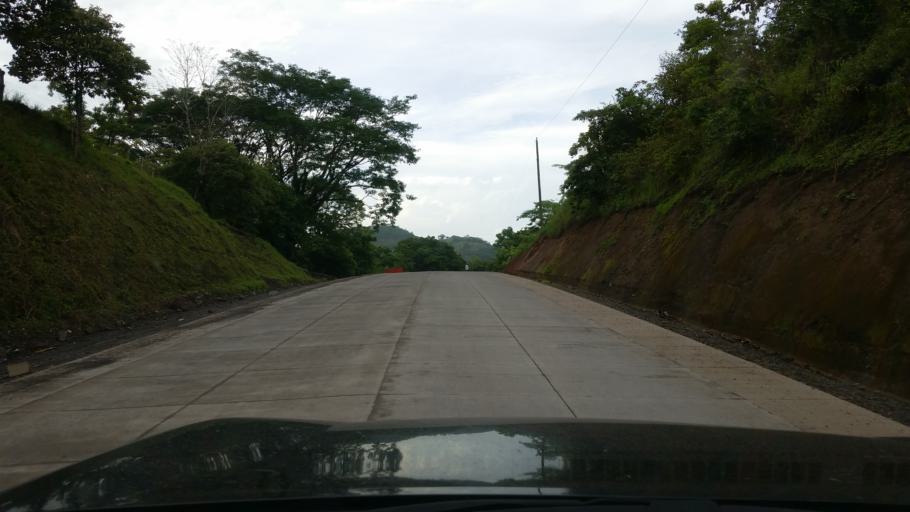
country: NI
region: Matagalpa
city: Rio Blanco
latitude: 12.9753
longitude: -85.1514
